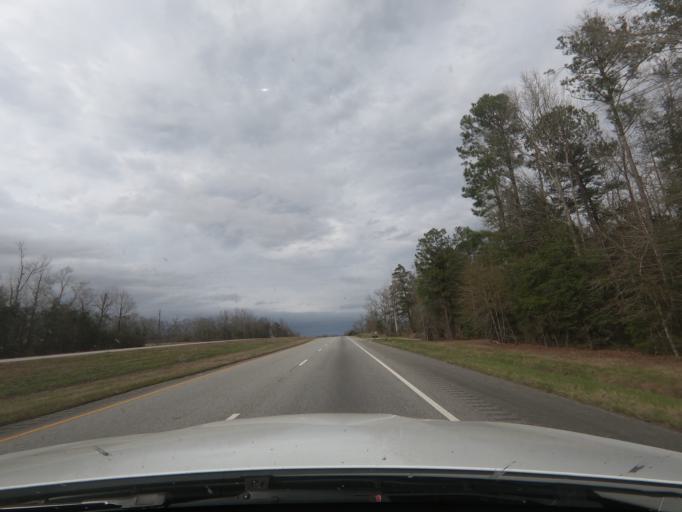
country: US
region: Alabama
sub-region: Russell County
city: Ladonia
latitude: 32.2541
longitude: -85.1632
